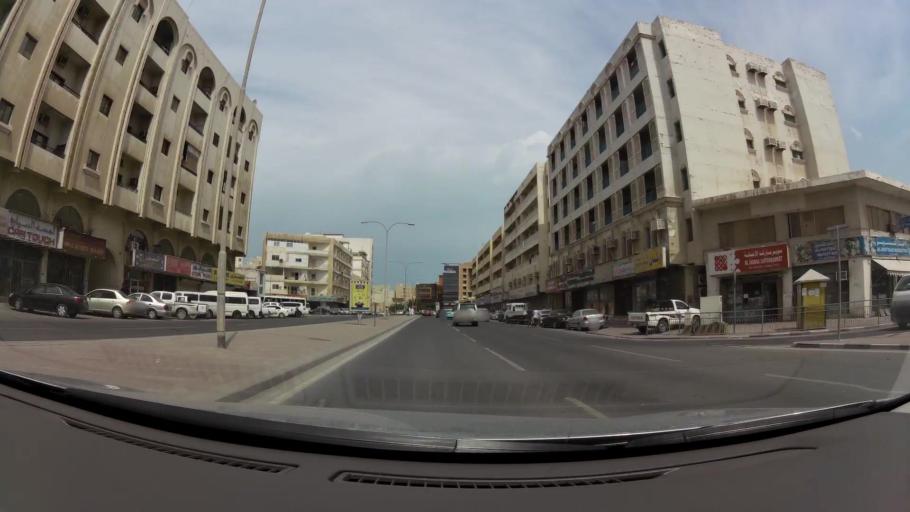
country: QA
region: Baladiyat ad Dawhah
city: Doha
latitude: 25.2785
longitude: 51.5423
